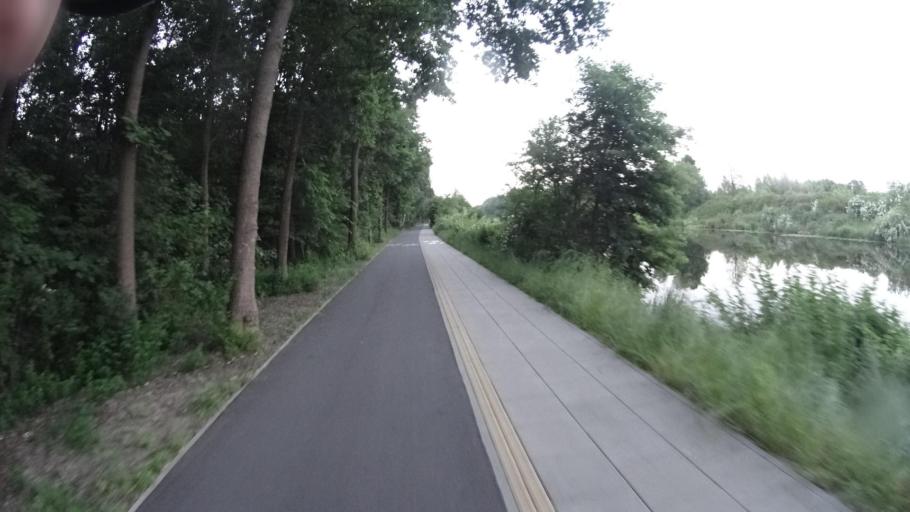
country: PL
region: Masovian Voivodeship
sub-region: Powiat legionowski
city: Stanislawow Pierwszy
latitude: 52.3916
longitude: 21.0380
